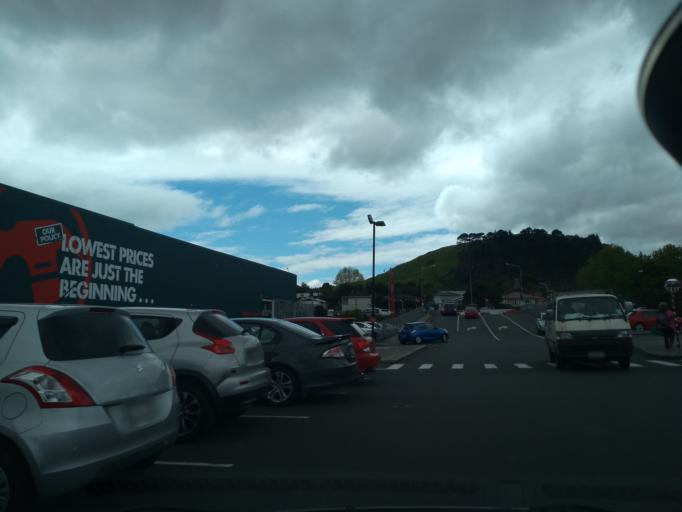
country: NZ
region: Auckland
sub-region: Auckland
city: Tamaki
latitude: -36.8981
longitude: 174.8425
